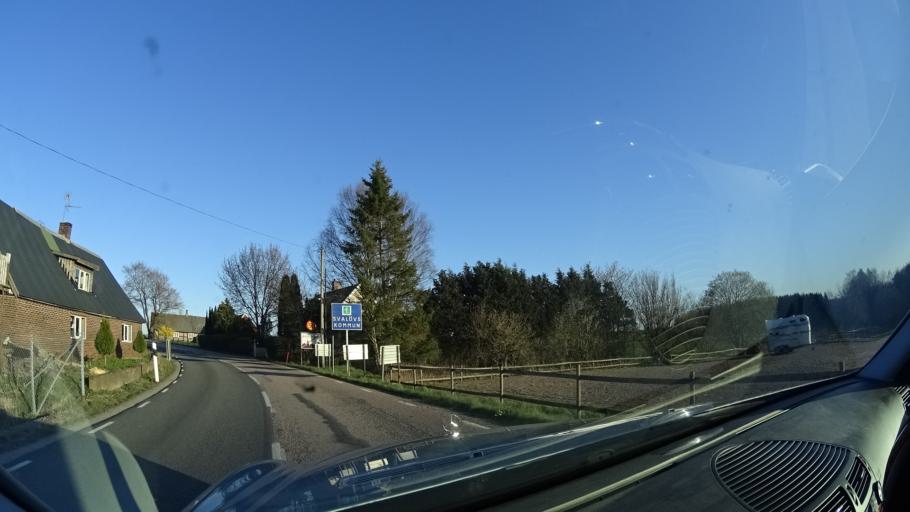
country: SE
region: Skane
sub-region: Bjuvs Kommun
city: Billesholm
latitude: 56.0412
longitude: 13.0126
